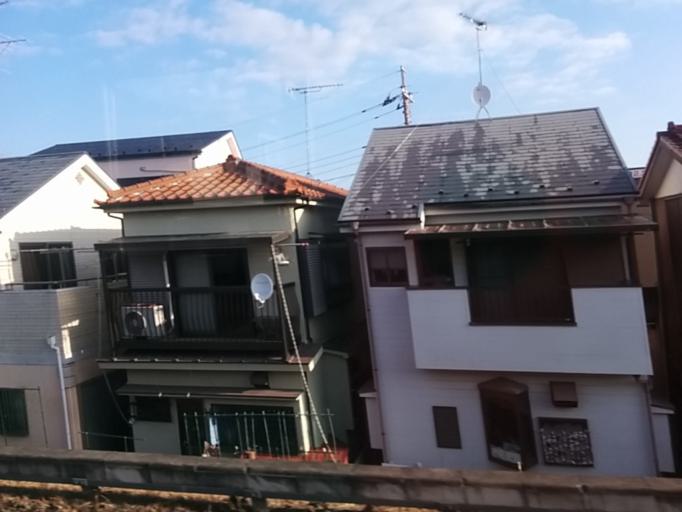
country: JP
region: Saitama
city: Oi
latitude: 35.8413
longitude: 139.5461
